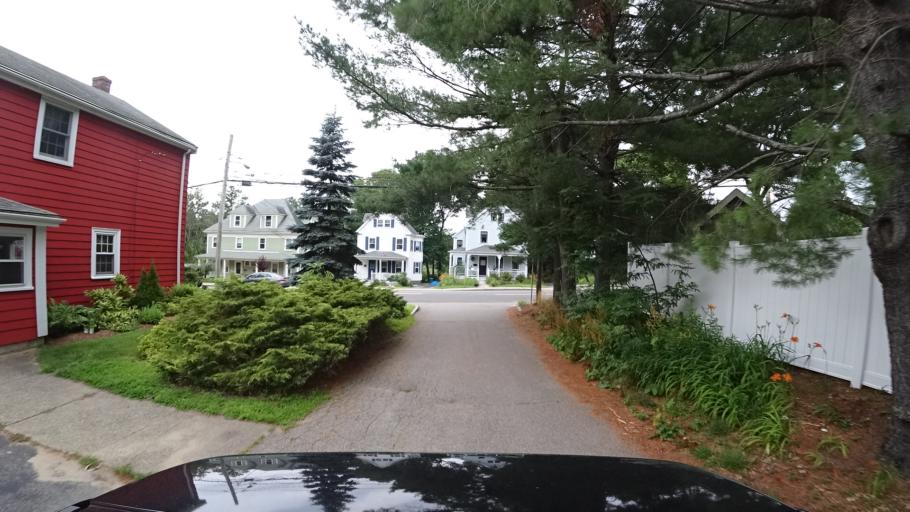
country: US
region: Massachusetts
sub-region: Norfolk County
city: Dedham
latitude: 42.2427
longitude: -71.1787
